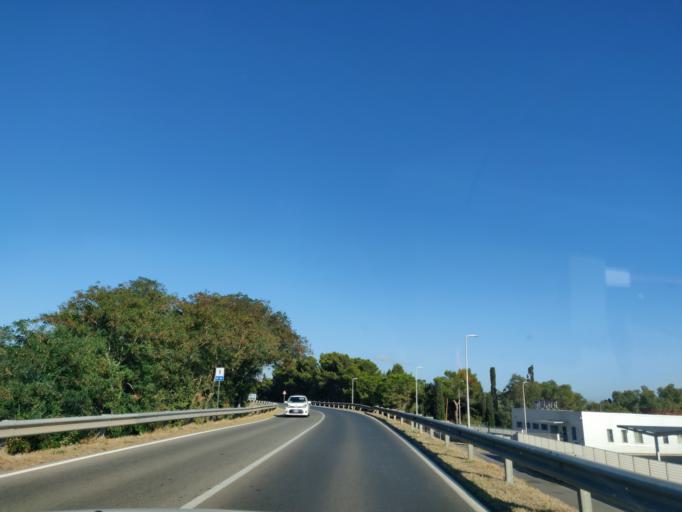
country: IT
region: Tuscany
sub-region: Provincia di Grosseto
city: Orbetello Scalo
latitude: 42.4469
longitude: 11.2456
